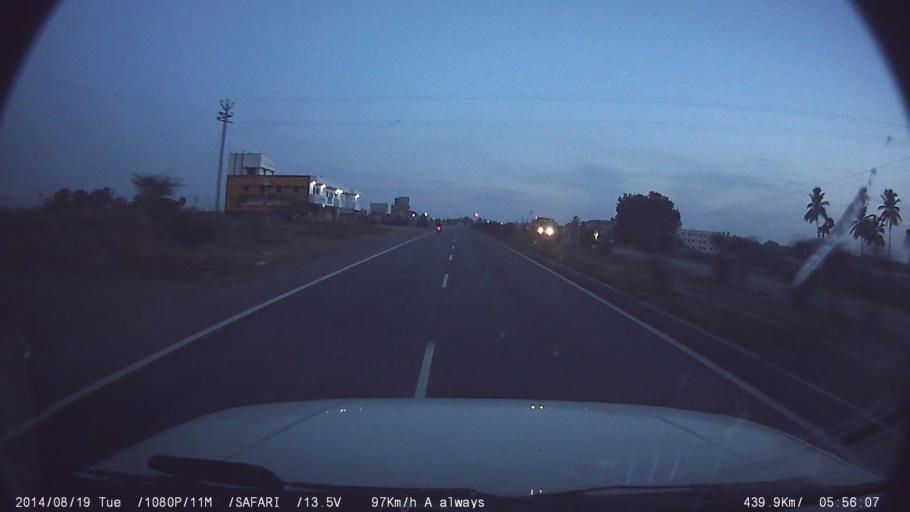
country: IN
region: Tamil Nadu
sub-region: Salem
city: Omalur
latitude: 11.7537
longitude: 78.0510
